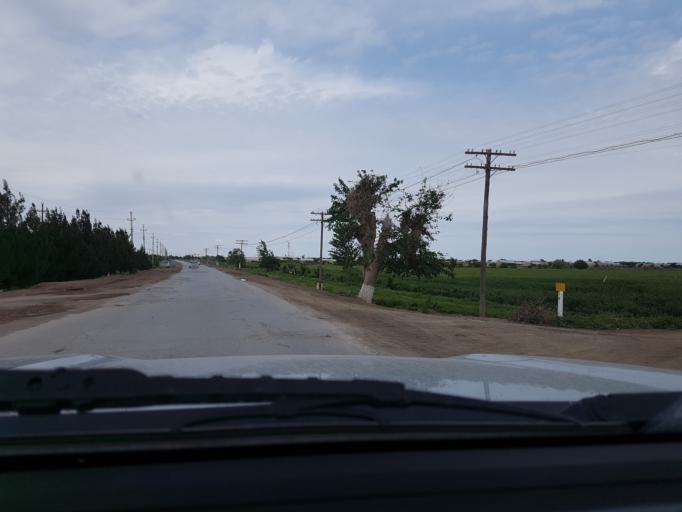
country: TM
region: Lebap
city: Sayat
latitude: 38.4638
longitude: 64.1749
